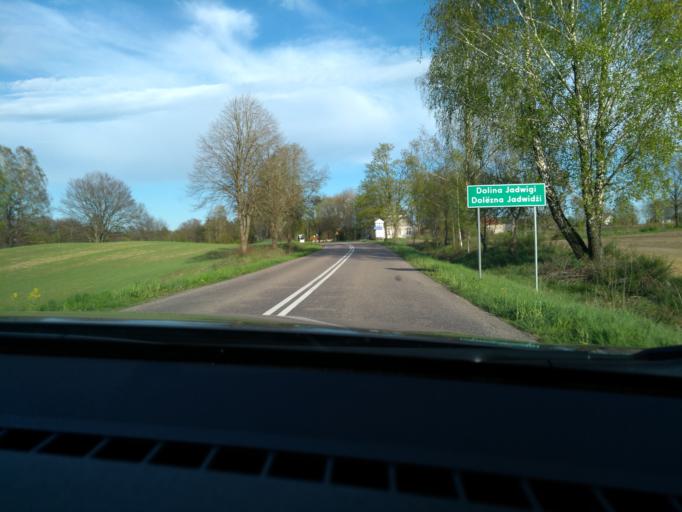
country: PL
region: Pomeranian Voivodeship
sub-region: Powiat leborski
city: Cewice
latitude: 54.3393
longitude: 17.7453
